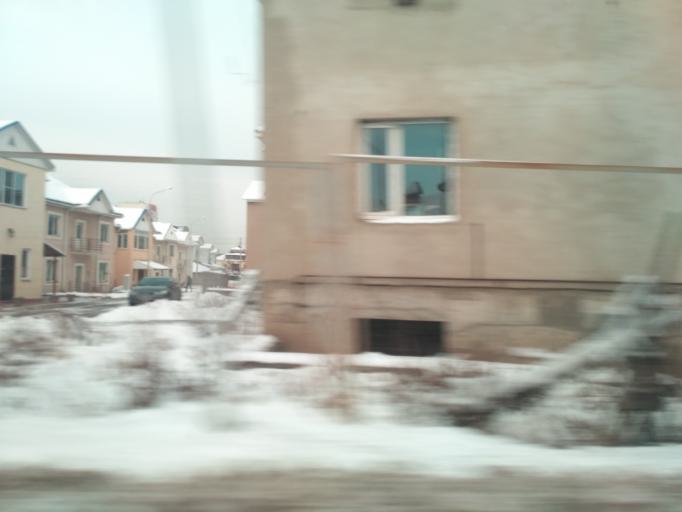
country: KZ
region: Almaty Qalasy
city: Almaty
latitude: 43.2167
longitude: 76.7921
